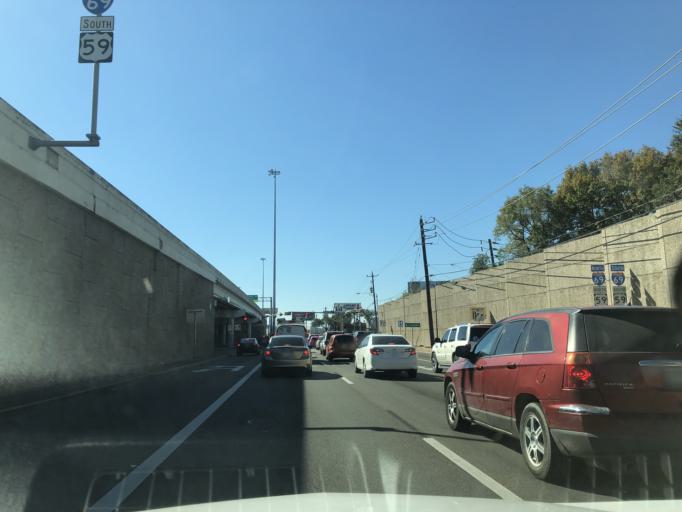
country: US
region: Texas
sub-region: Harris County
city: Piney Point Village
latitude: 29.6930
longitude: -95.5268
